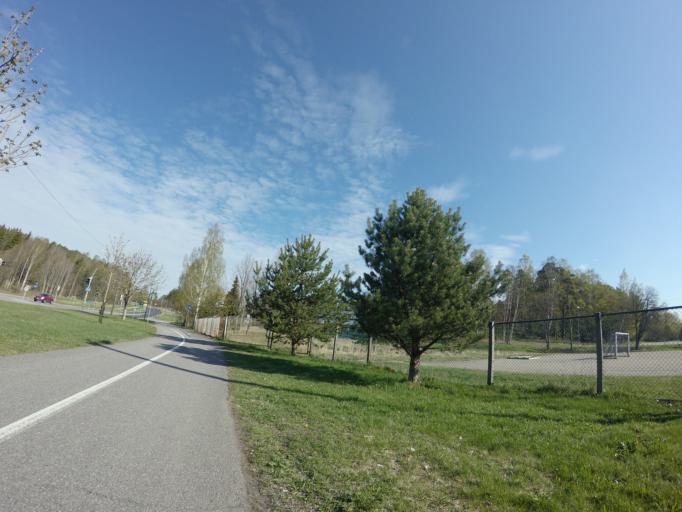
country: FI
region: Varsinais-Suomi
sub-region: Turku
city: Raisio
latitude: 60.4526
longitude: 22.1584
